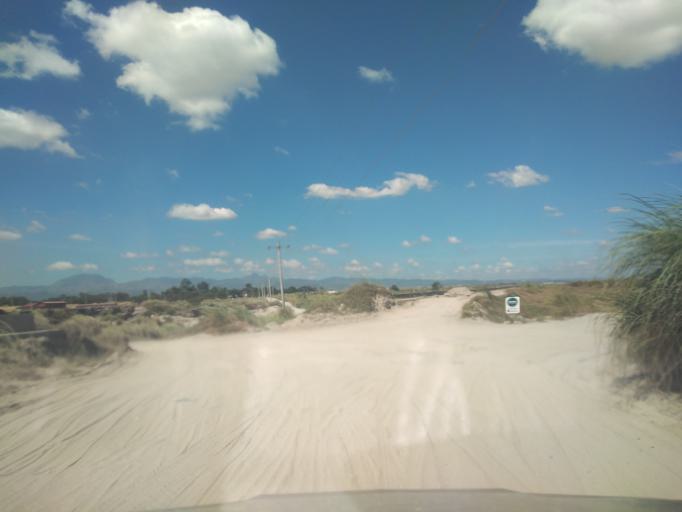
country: PH
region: Central Luzon
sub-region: Province of Pampanga
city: Balas
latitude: 15.0597
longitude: 120.5954
